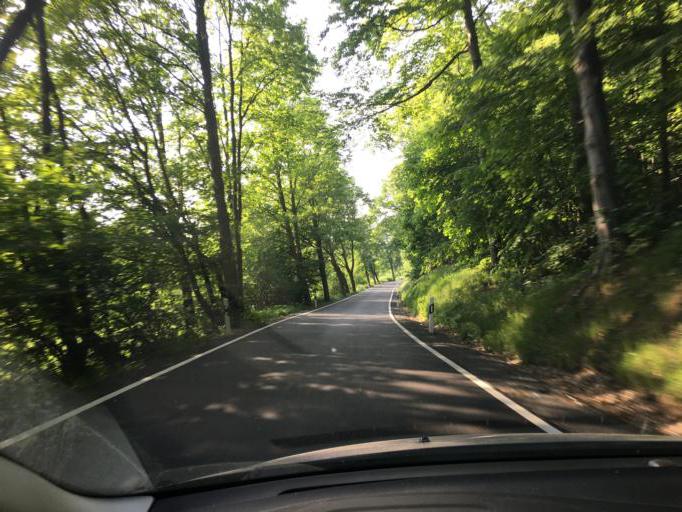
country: DE
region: Saxony
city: Colditz
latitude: 51.1172
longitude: 12.8104
